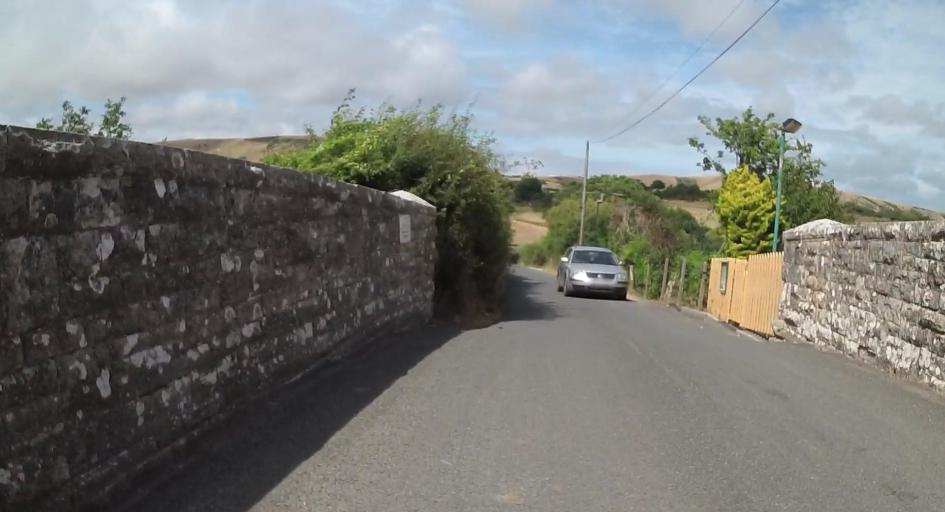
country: GB
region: England
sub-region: Dorset
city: Swanage
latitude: 50.6131
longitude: -1.9813
